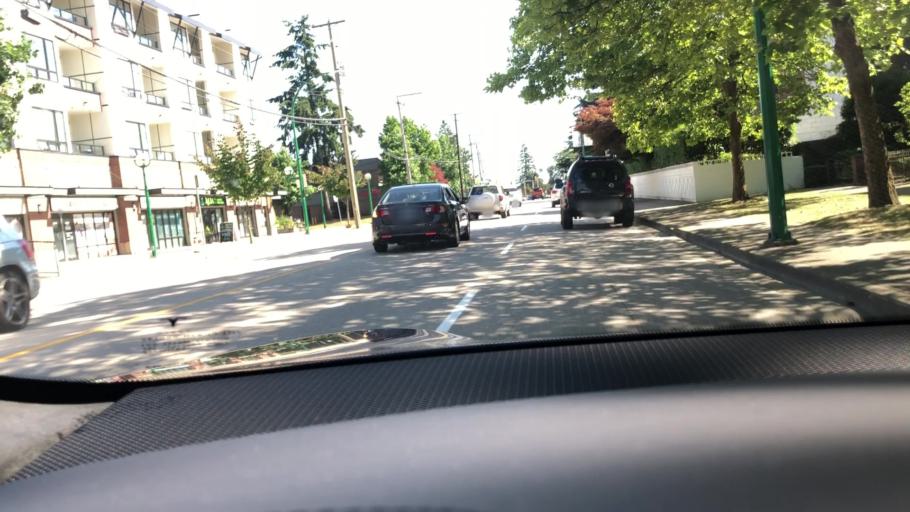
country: CA
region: British Columbia
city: Burnaby
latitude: 49.2243
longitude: -122.9890
